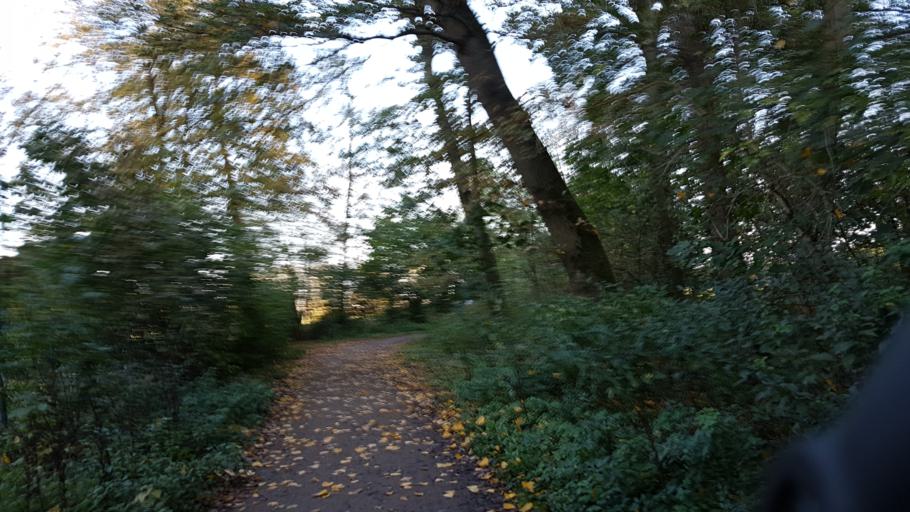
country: DE
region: Lower Saxony
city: Hemmingen
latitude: 52.3219
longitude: 9.7007
